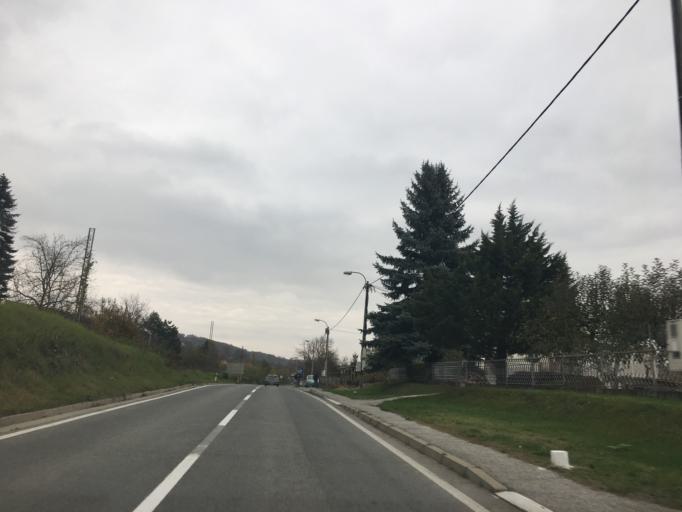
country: RS
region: Central Serbia
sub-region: Raski Okrug
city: Kraljevo
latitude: 43.7278
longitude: 20.7552
